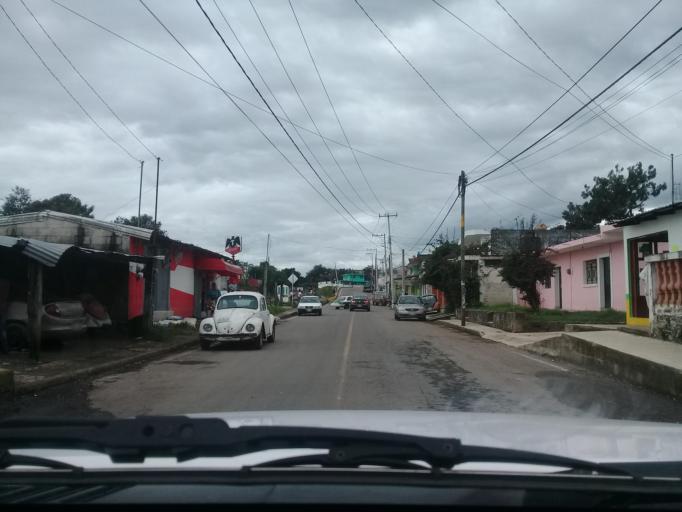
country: MX
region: Veracruz
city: Rafael Lucio
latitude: 19.5969
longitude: -96.9892
